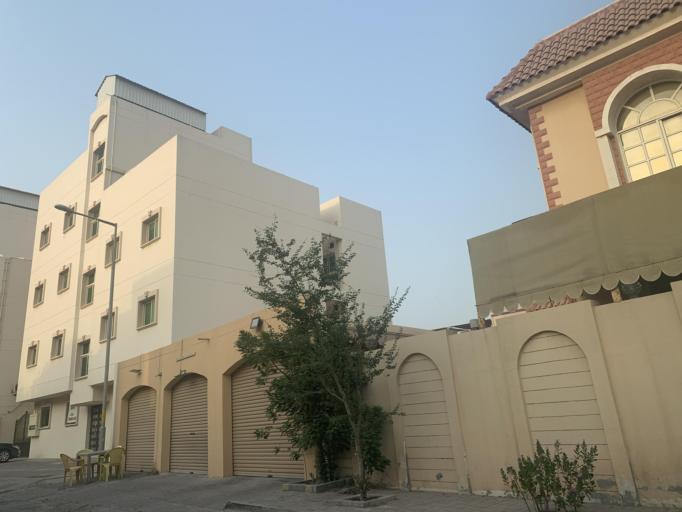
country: BH
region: Manama
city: Jidd Hafs
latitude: 26.2247
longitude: 50.5176
